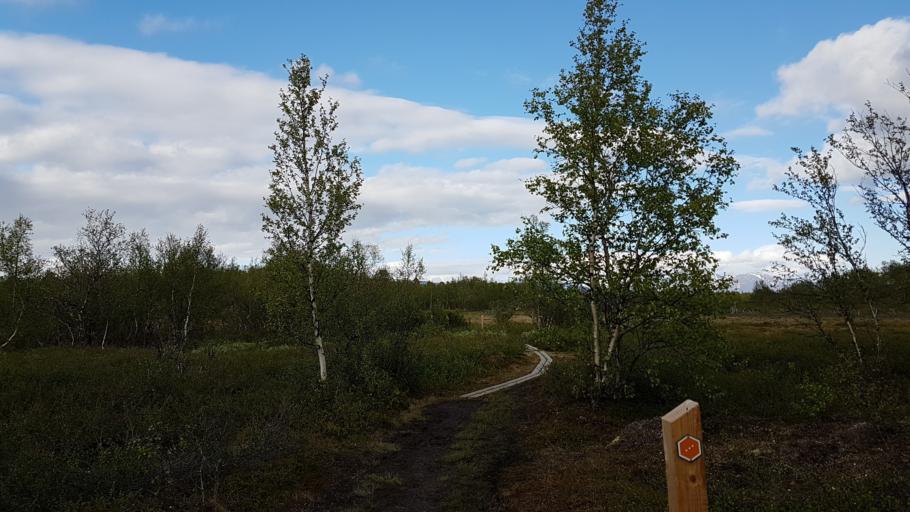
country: NO
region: Troms
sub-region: Bardu
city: Setermoen
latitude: 68.3414
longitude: 18.7705
